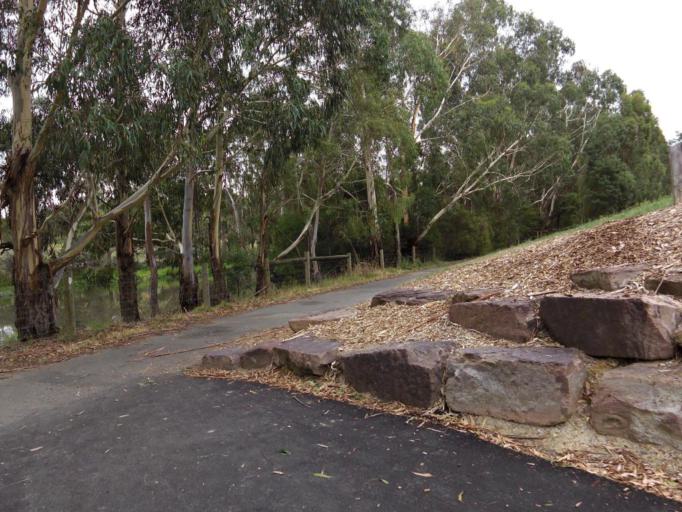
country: AU
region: Victoria
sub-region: Manningham
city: Doncaster
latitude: -37.7739
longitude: 145.1351
